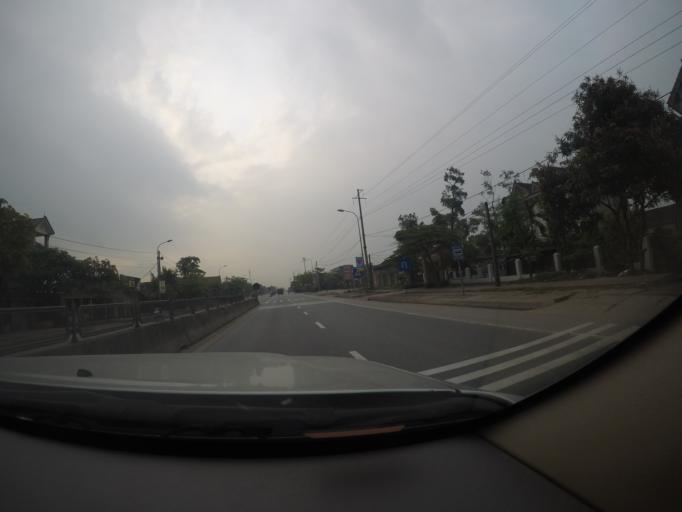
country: VN
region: Ha Tinh
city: Cam Xuyen
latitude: 18.2448
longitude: 106.0090
